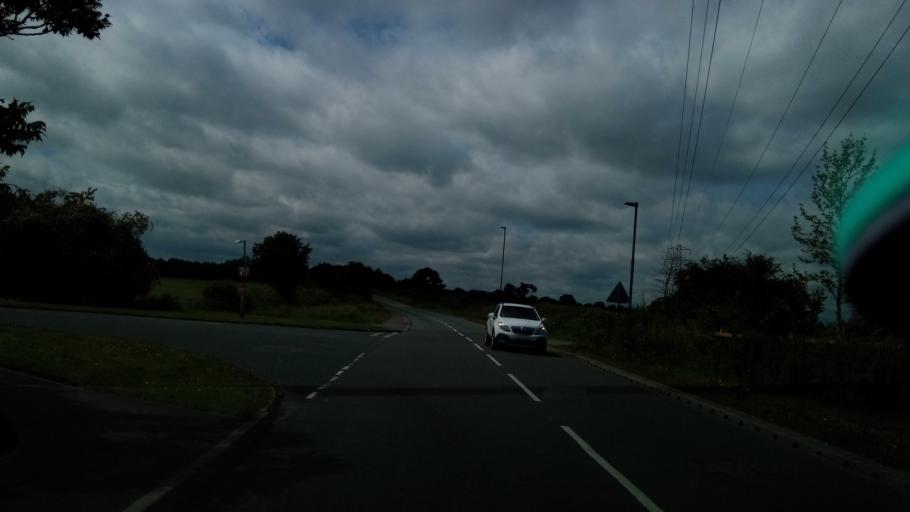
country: GB
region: England
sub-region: Derbyshire
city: Findern
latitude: 52.8734
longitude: -1.5083
